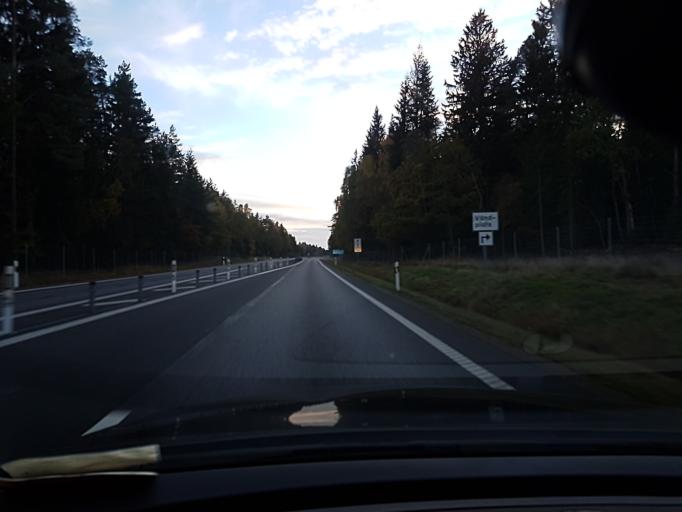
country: SE
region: Kronoberg
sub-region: Ljungby Kommun
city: Ljungby
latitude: 56.7751
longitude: 13.8115
